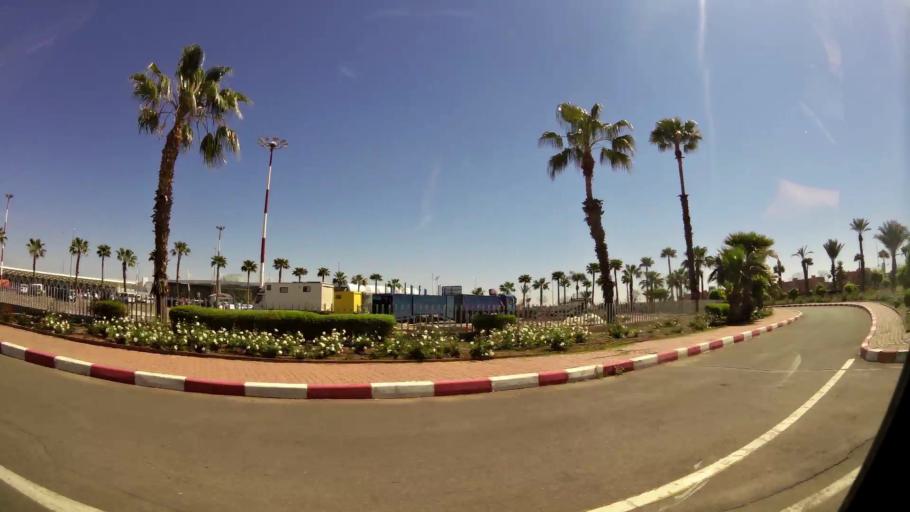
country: MA
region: Marrakech-Tensift-Al Haouz
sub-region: Marrakech
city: Marrakesh
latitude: 31.5979
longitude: -8.0270
